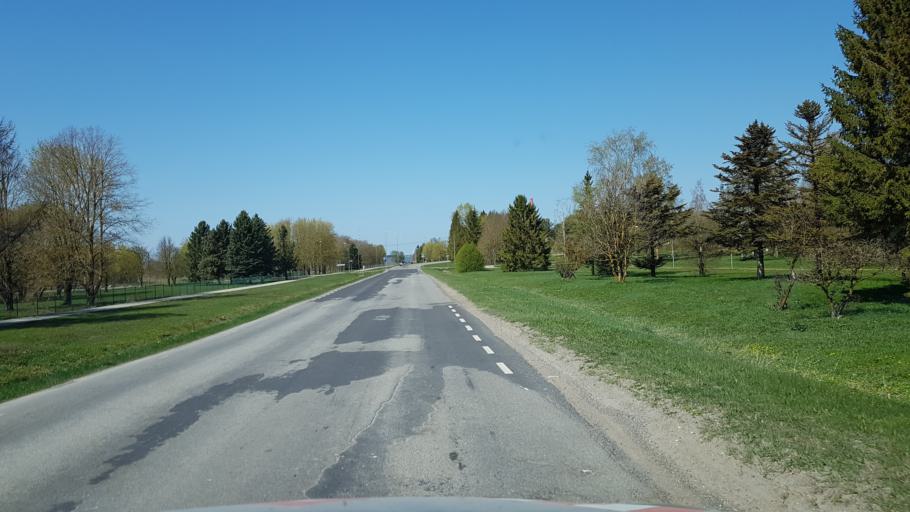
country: EE
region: Harju
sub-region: Joelaehtme vald
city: Loo
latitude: 59.4307
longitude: 24.9412
